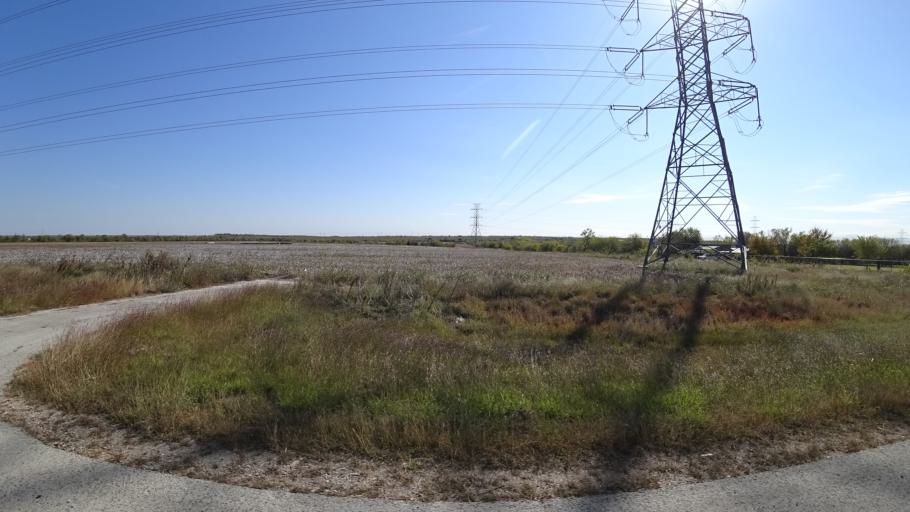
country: US
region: Texas
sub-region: Travis County
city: Onion Creek
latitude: 30.0856
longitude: -97.6854
